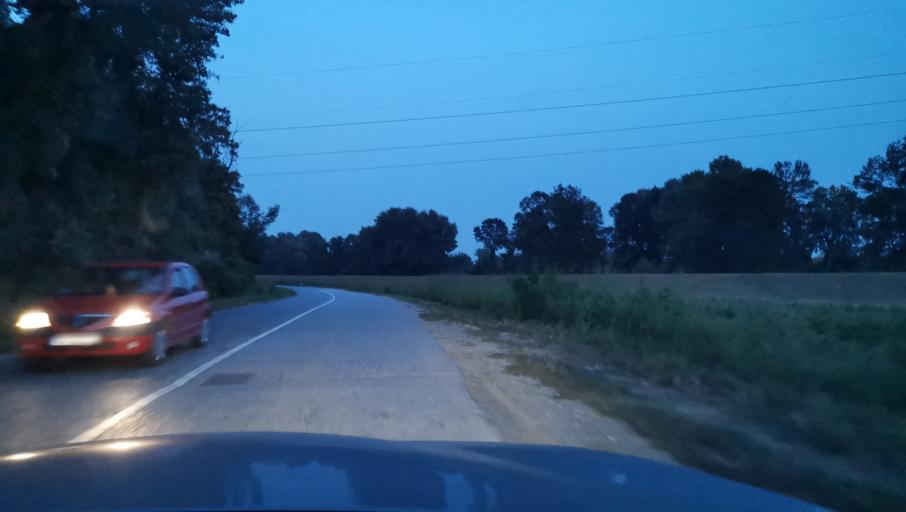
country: RS
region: Central Serbia
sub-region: Belgrade
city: Obrenovac
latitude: 44.6766
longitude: 20.1756
